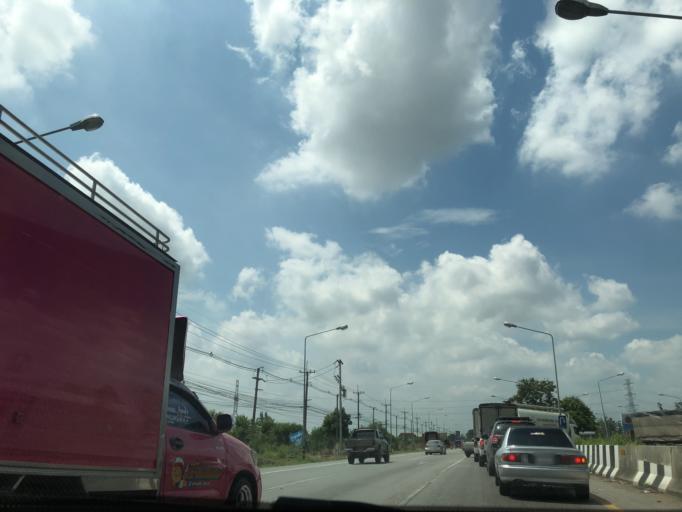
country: TH
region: Pathum Thani
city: Lat Lum Kaeo
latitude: 14.0175
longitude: 100.3613
